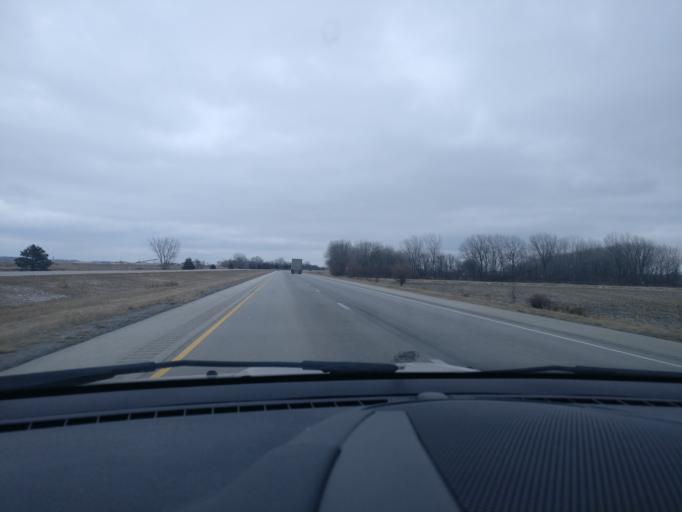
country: US
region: Iowa
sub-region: Scott County
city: Le Claire
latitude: 41.5394
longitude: -90.2904
